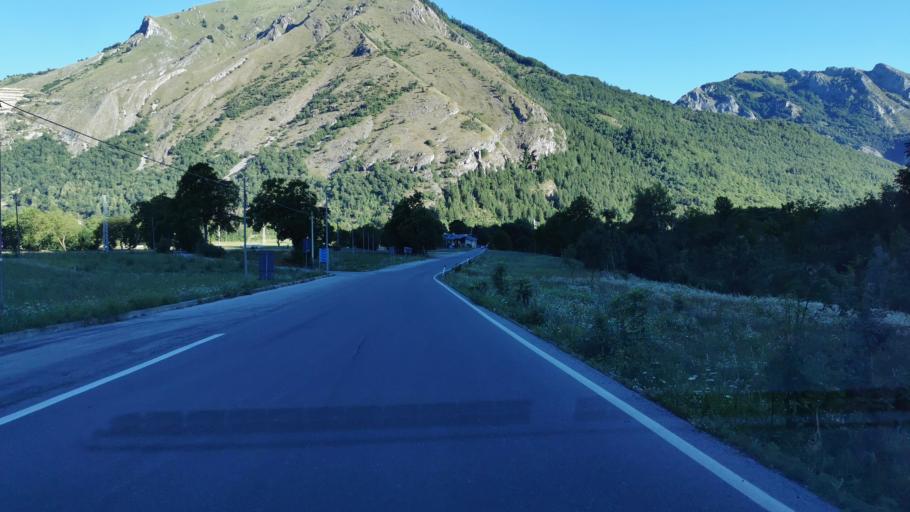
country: IT
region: Piedmont
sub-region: Provincia di Cuneo
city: Entracque
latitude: 44.2555
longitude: 7.3850
